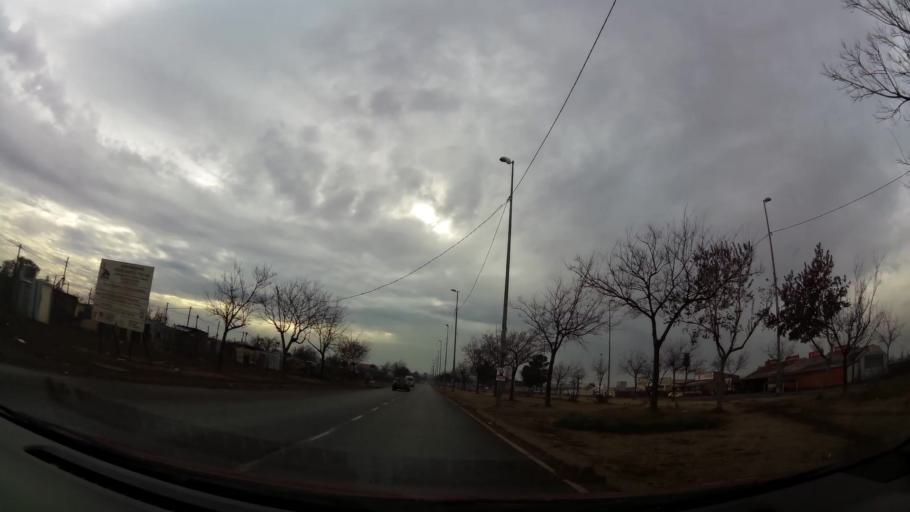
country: ZA
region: Gauteng
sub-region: City of Johannesburg Metropolitan Municipality
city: Soweto
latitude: -26.2900
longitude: 27.8448
